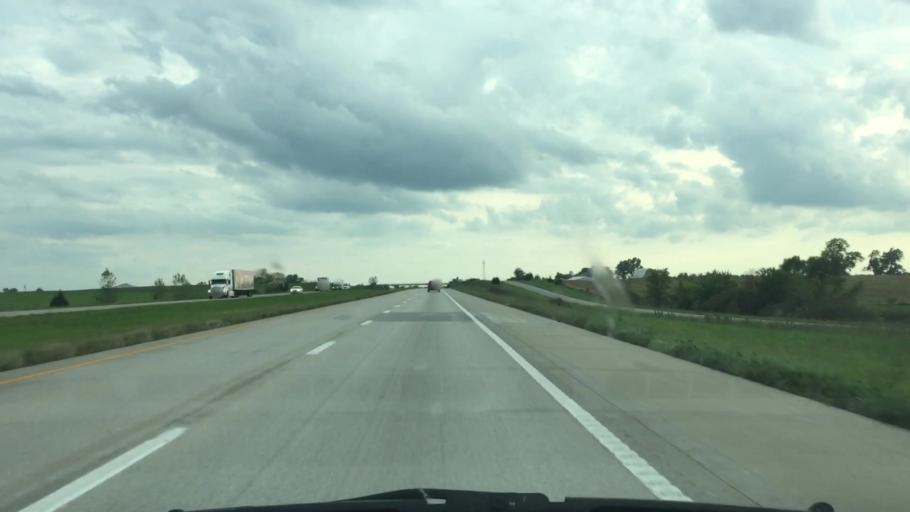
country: US
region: Missouri
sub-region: Clinton County
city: Lathrop
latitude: 39.5927
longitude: -94.2560
